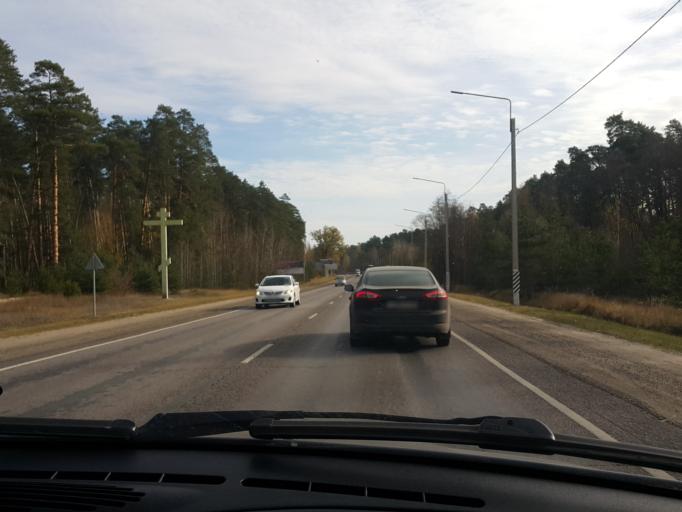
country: RU
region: Tambov
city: Donskoye
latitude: 52.7086
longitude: 41.5348
